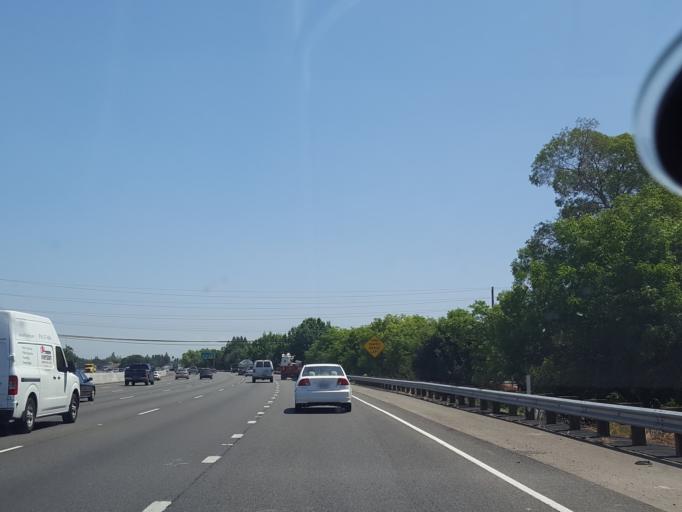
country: US
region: California
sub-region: Sacramento County
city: La Riviera
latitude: 38.5621
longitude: -121.3462
